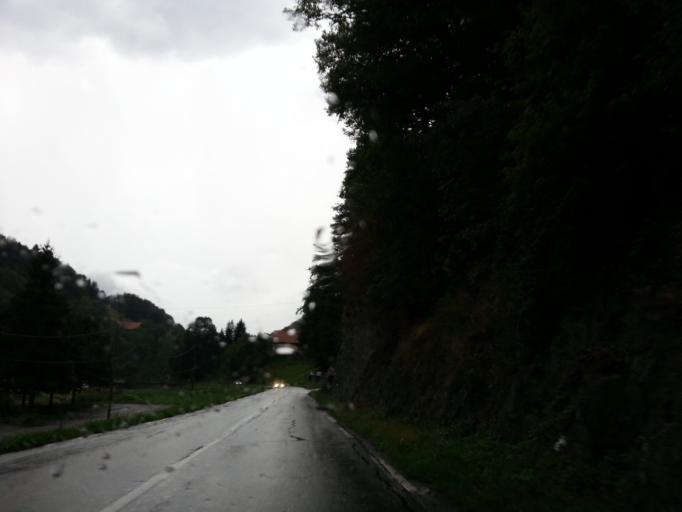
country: FR
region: Rhone-Alpes
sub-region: Departement de la Savoie
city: Marthod
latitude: 45.7165
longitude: 6.4461
